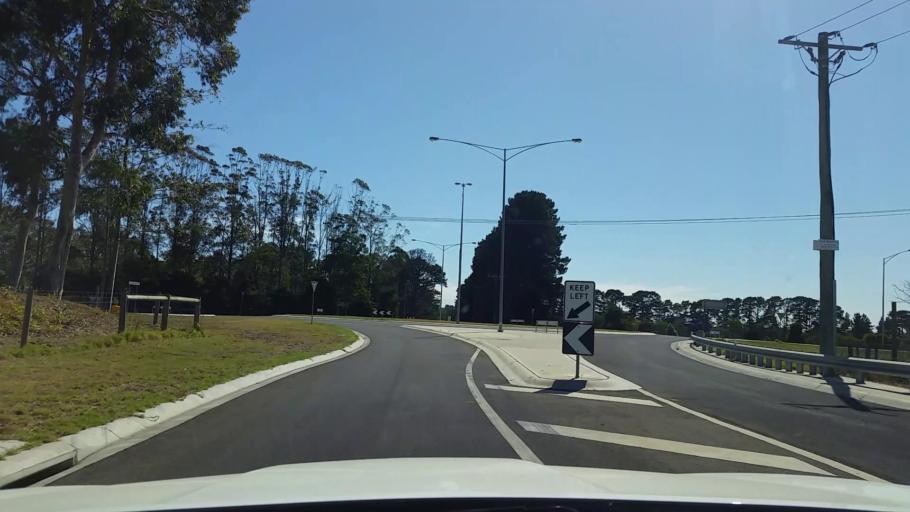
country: AU
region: Victoria
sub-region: Mornington Peninsula
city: Hastings
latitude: -38.3008
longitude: 145.1456
